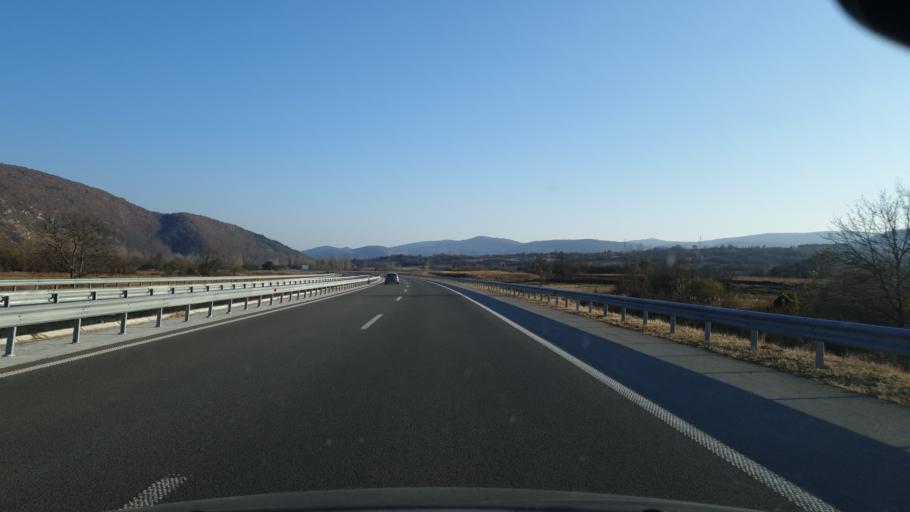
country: RS
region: Central Serbia
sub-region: Pirotski Okrug
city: Dimitrovgrad
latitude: 43.0424
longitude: 22.7087
